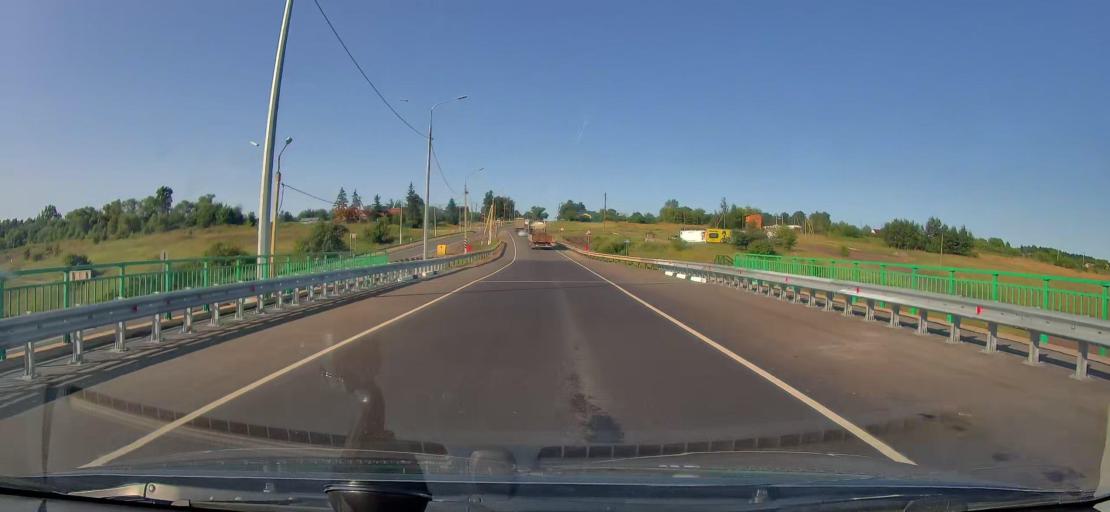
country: RU
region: Orjol
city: Mtsensk
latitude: 53.1875
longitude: 36.4187
